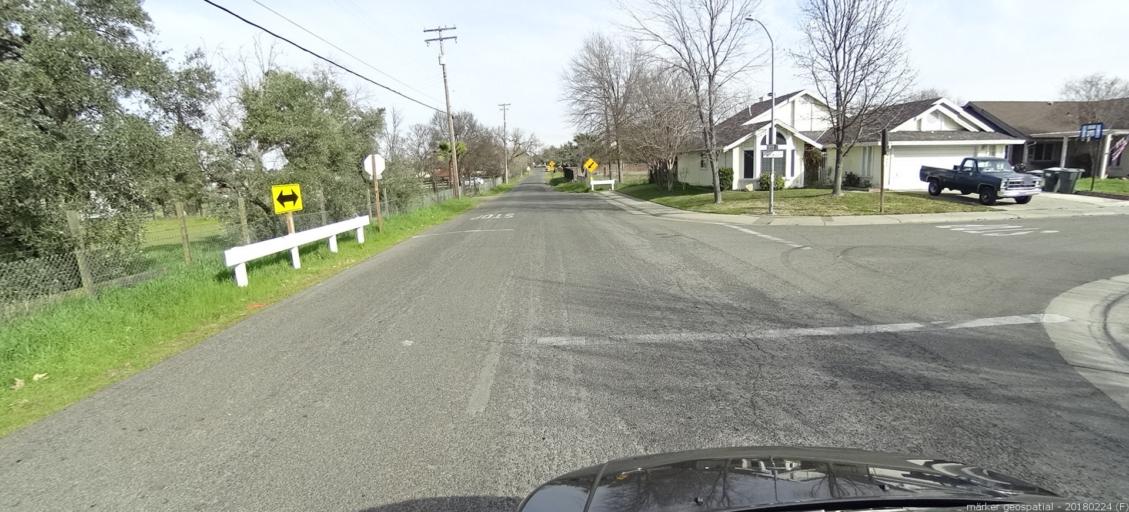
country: US
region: California
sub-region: Sacramento County
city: Rio Linda
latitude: 38.6935
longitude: -121.4615
